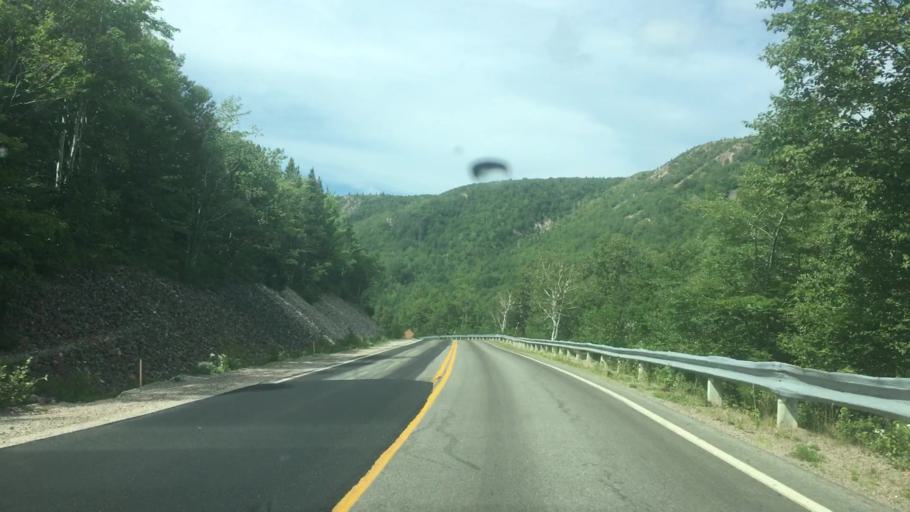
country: CA
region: Nova Scotia
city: Sydney Mines
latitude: 46.5790
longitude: -60.3896
